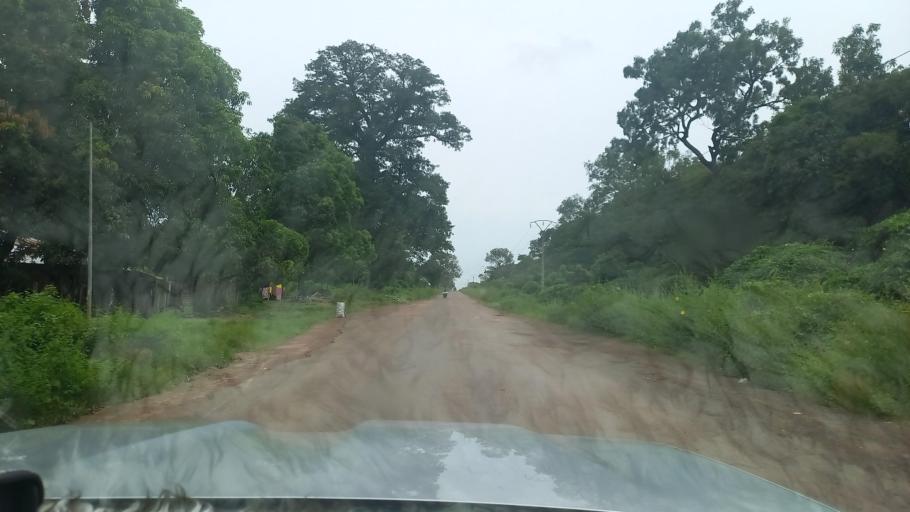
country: SN
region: Ziguinchor
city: Bignona
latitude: 12.8263
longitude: -16.1712
